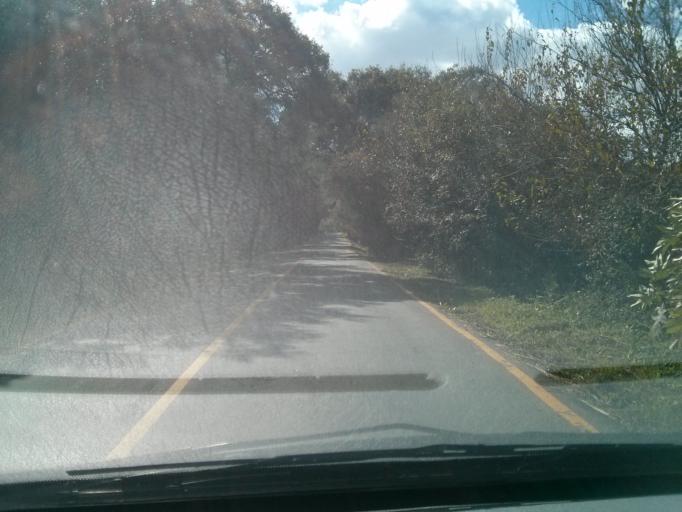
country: BR
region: Parana
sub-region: Sao Jose Dos Pinhais
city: Sao Jose dos Pinhais
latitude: -25.5509
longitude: -49.2252
